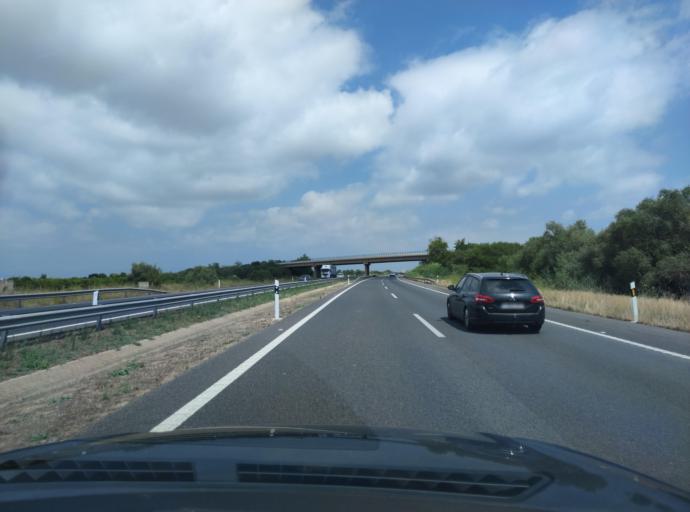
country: ES
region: Valencia
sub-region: Provincia de Castello
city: Vinaros
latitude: 40.4892
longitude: 0.4152
